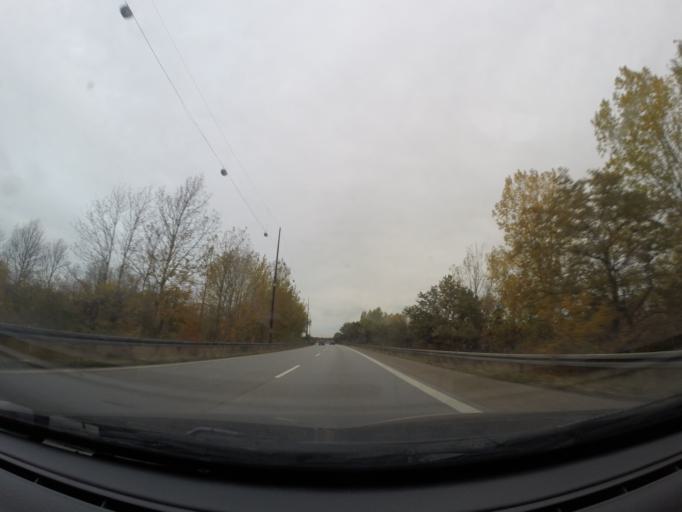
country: DK
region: Capital Region
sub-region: Ishoj Kommune
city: Ishoj
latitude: 55.6397
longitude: 12.3366
